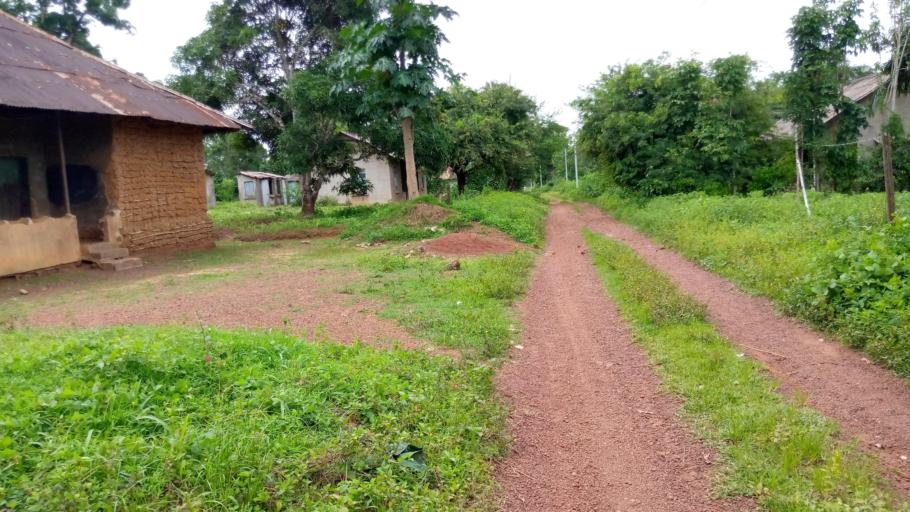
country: SL
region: Southern Province
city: Rotifunk
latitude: 8.1907
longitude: -12.5670
